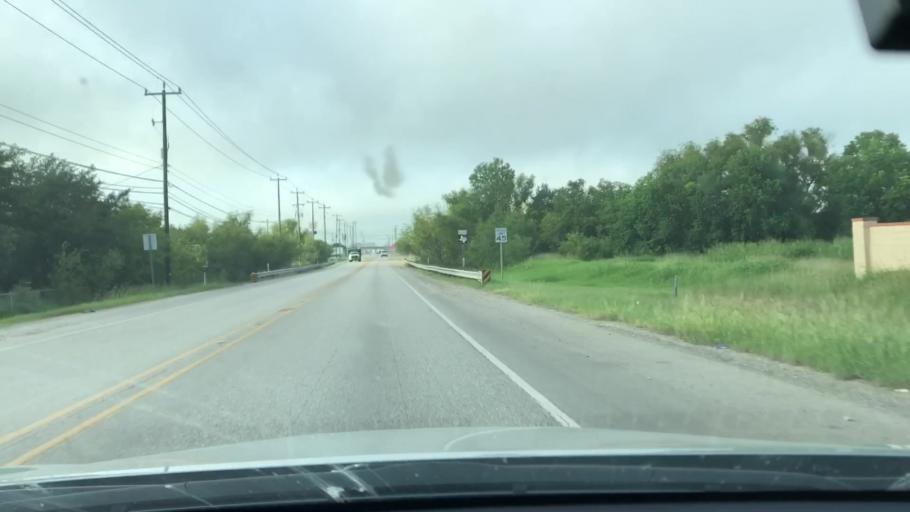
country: US
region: Texas
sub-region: Bexar County
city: Converse
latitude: 29.4641
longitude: -98.3155
